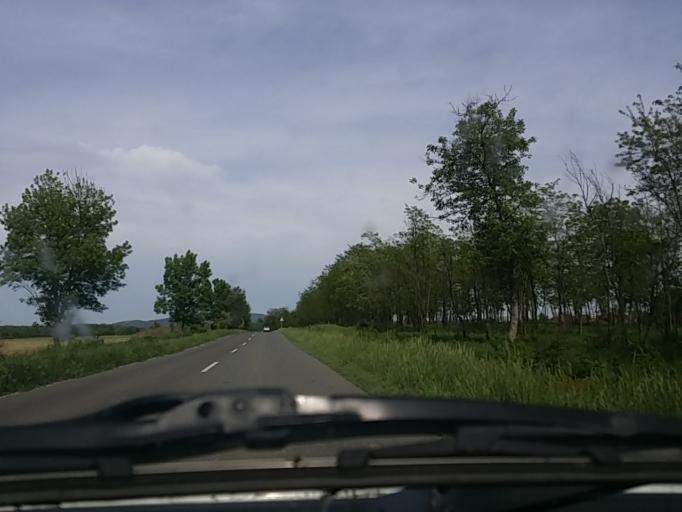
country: HU
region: Baranya
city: Harkany
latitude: 45.8392
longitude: 18.1392
